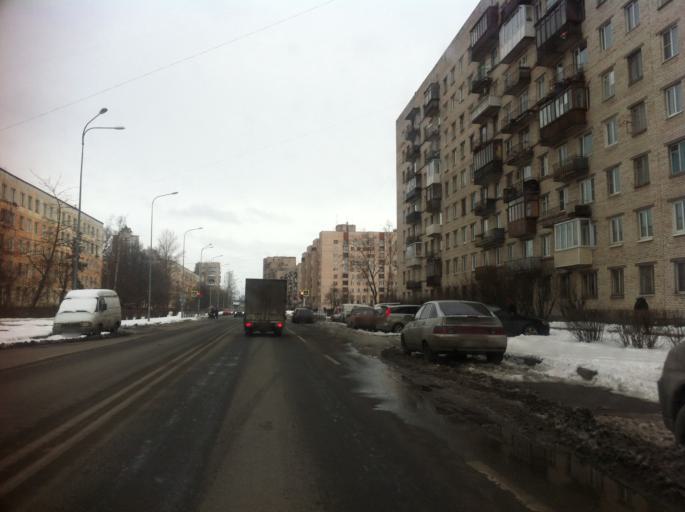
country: RU
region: St.-Petersburg
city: Dachnoye
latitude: 59.8453
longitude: 30.2315
